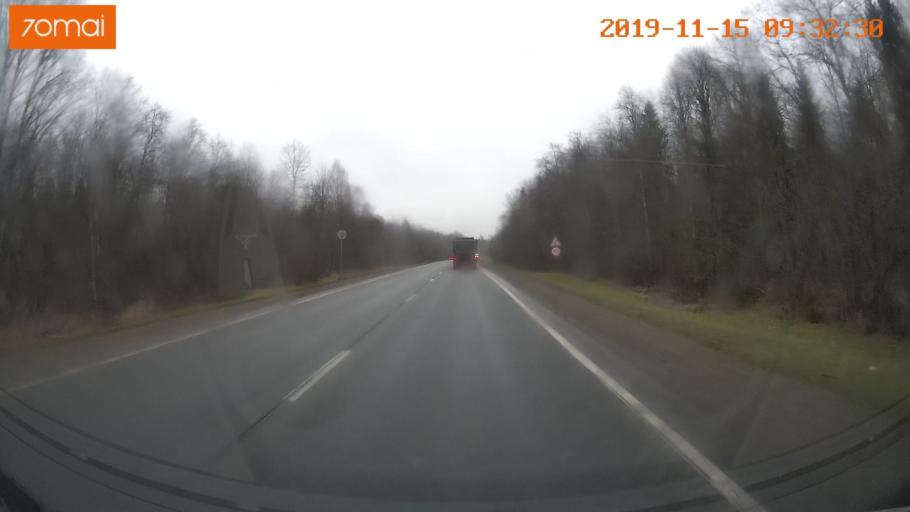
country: RU
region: Vologda
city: Sheksna
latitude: 59.2714
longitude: 38.3367
